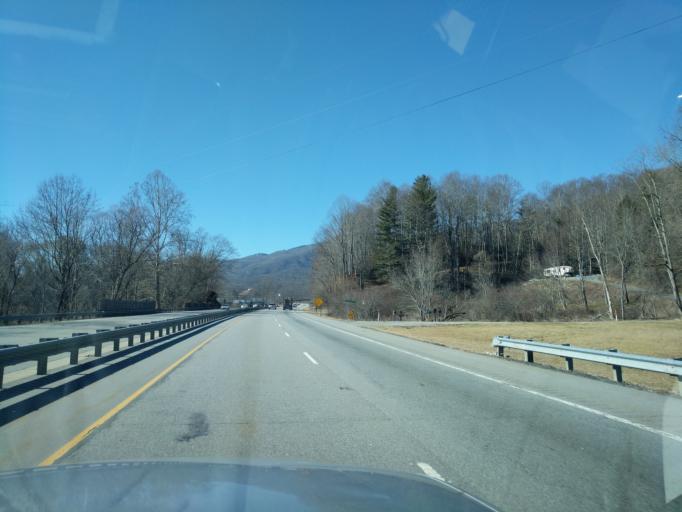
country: US
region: North Carolina
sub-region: Haywood County
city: Hazelwood
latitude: 35.4560
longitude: -83.0375
